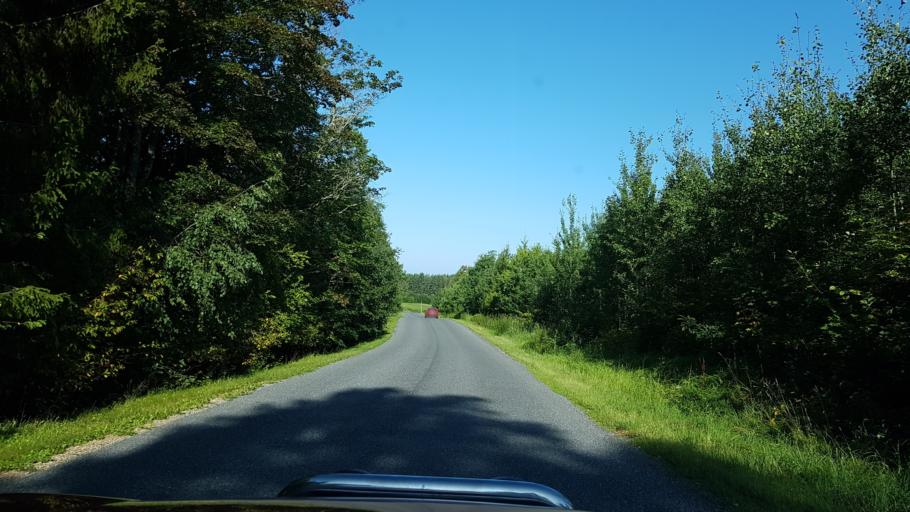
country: EE
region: Vorumaa
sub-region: Voru linn
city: Voru
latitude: 57.7371
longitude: 26.9256
